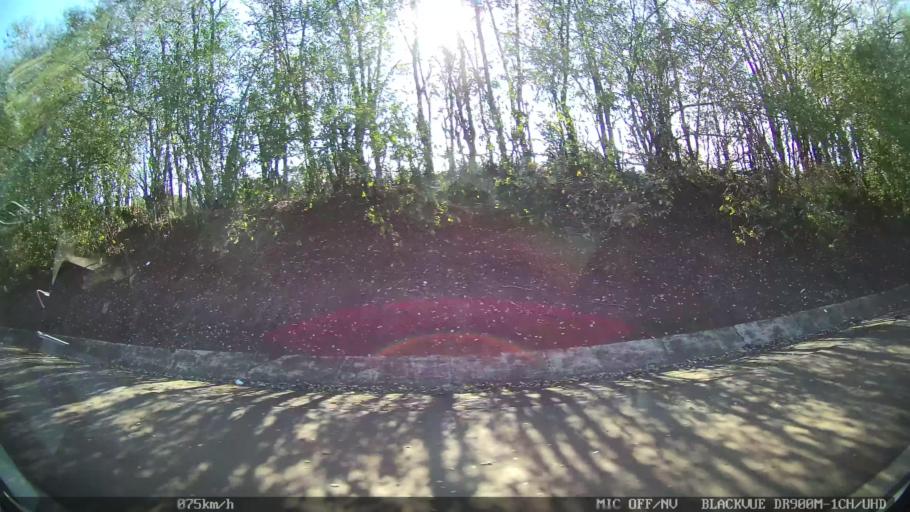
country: BR
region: Sao Paulo
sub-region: Iracemapolis
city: Iracemapolis
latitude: -22.6640
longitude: -47.5333
